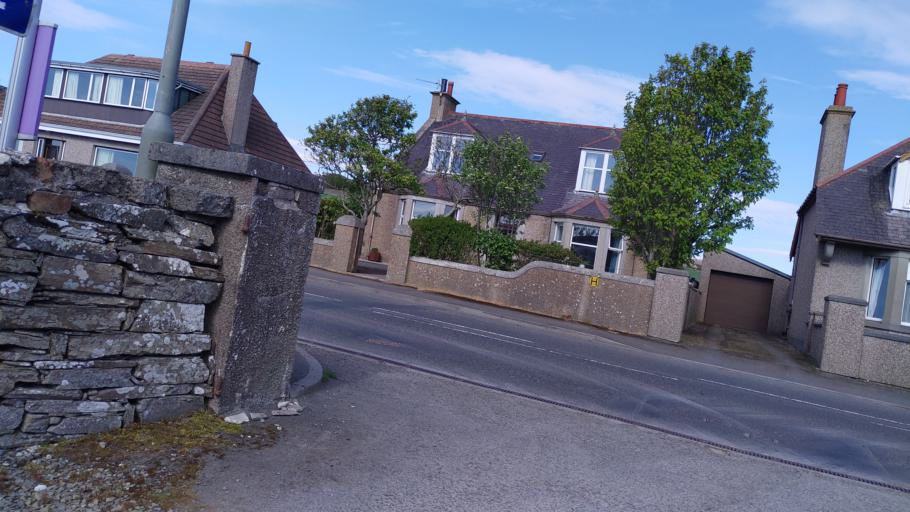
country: GB
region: Scotland
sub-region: Orkney Islands
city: Orkney
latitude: 58.9752
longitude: -2.9700
